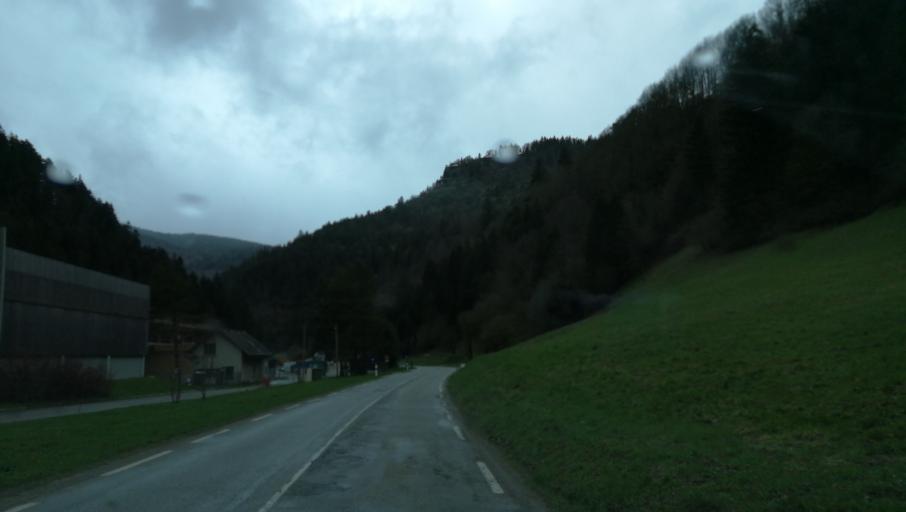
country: FR
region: Rhone-Alpes
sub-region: Departement de l'Isere
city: Villard-de-Lans
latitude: 45.0807
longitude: 5.5336
